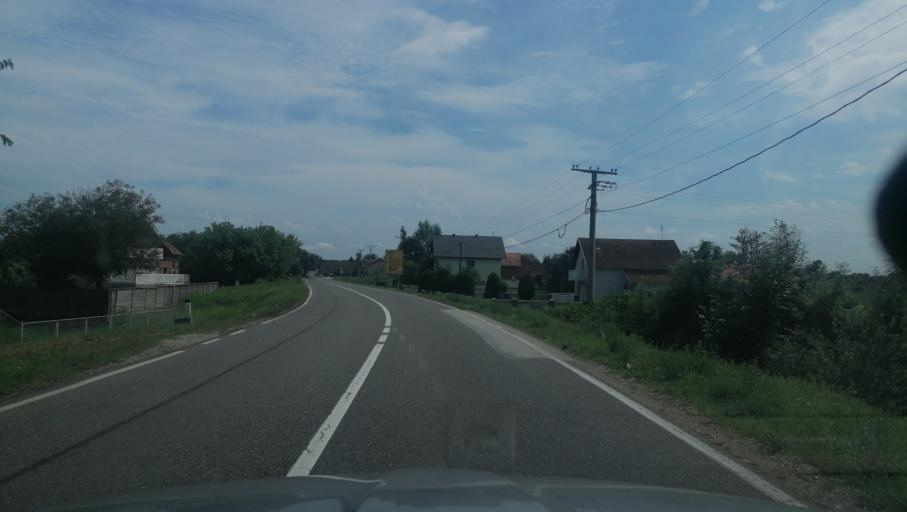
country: HR
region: Brodsko-Posavska
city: Krusevica
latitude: 45.0364
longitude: 18.5141
